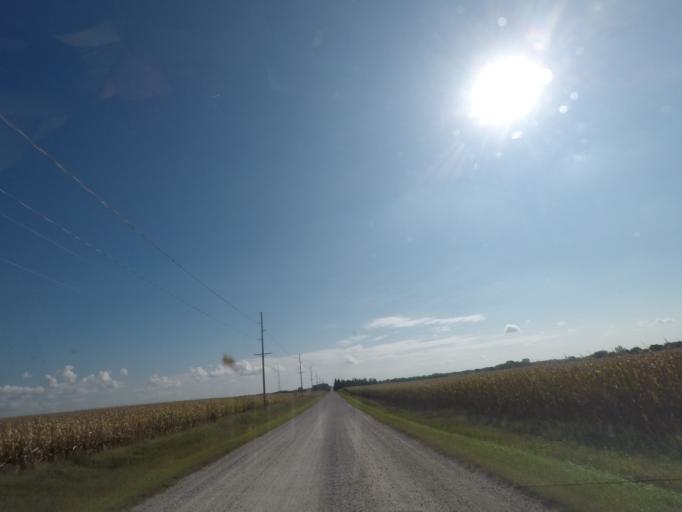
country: US
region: Iowa
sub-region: Story County
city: Nevada
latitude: 42.0348
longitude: -93.4048
